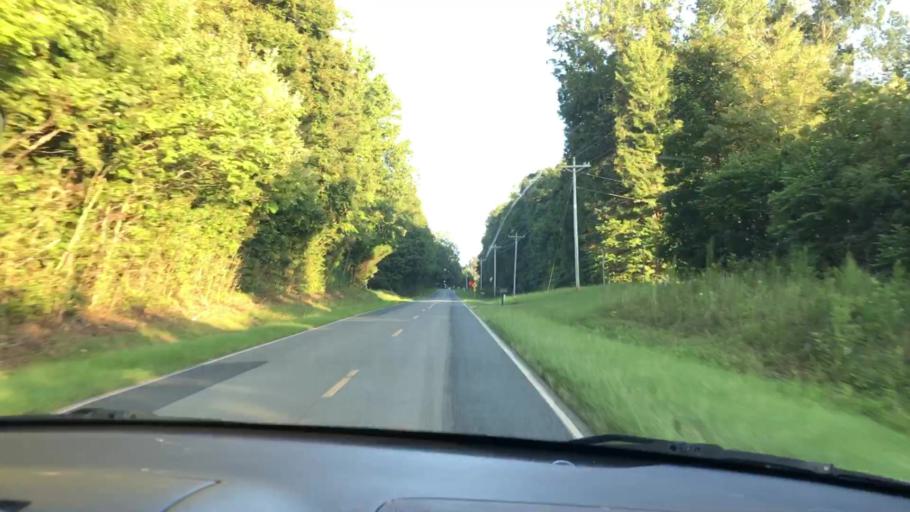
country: US
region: North Carolina
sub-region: Randolph County
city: Franklinville
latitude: 35.8080
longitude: -79.6864
